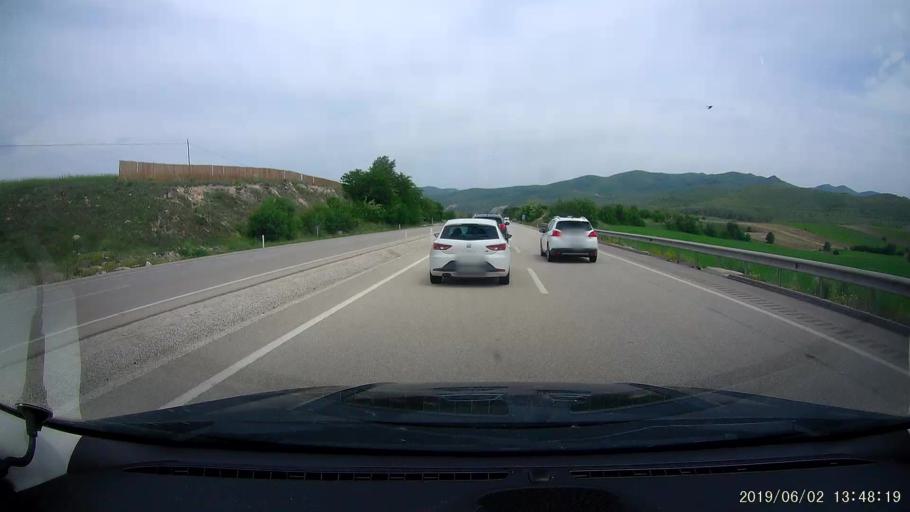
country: TR
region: Cankiri
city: Kursunlu
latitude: 40.8359
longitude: 33.3033
